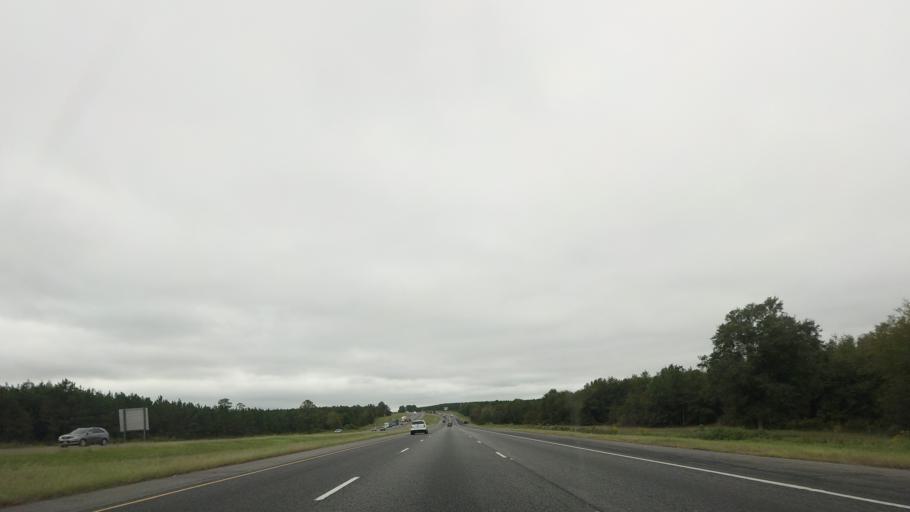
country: US
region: Georgia
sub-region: Turner County
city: Ashburn
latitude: 31.8146
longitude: -83.7087
